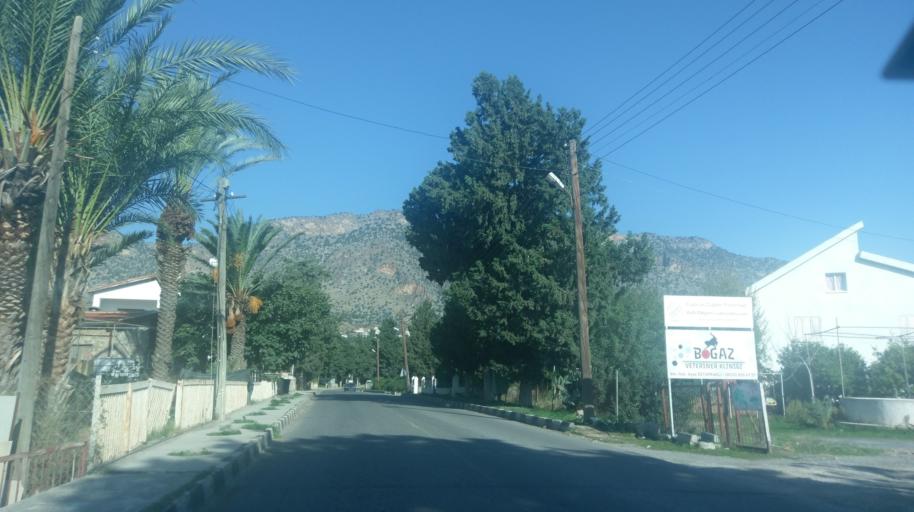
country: CY
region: Keryneia
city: Kyrenia
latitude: 35.2863
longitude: 33.2800
